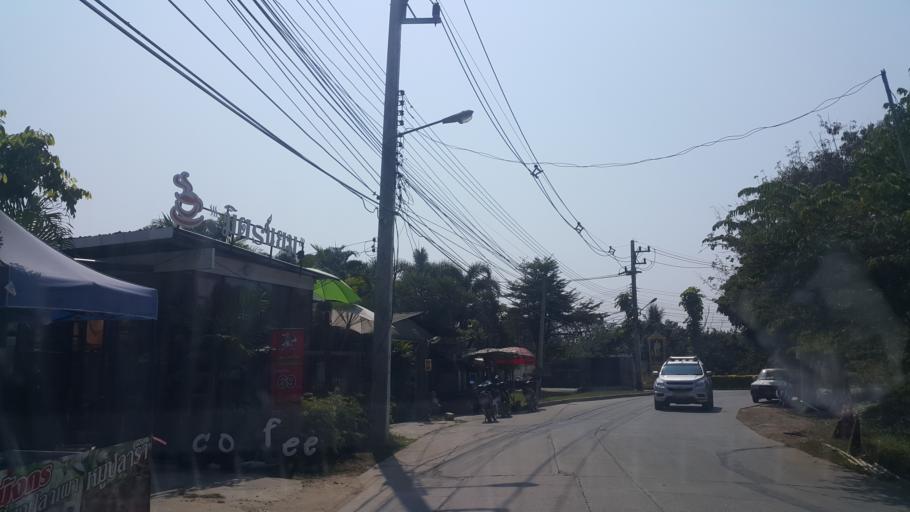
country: TH
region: Chiang Mai
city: Saraphi
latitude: 18.7354
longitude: 99.0736
